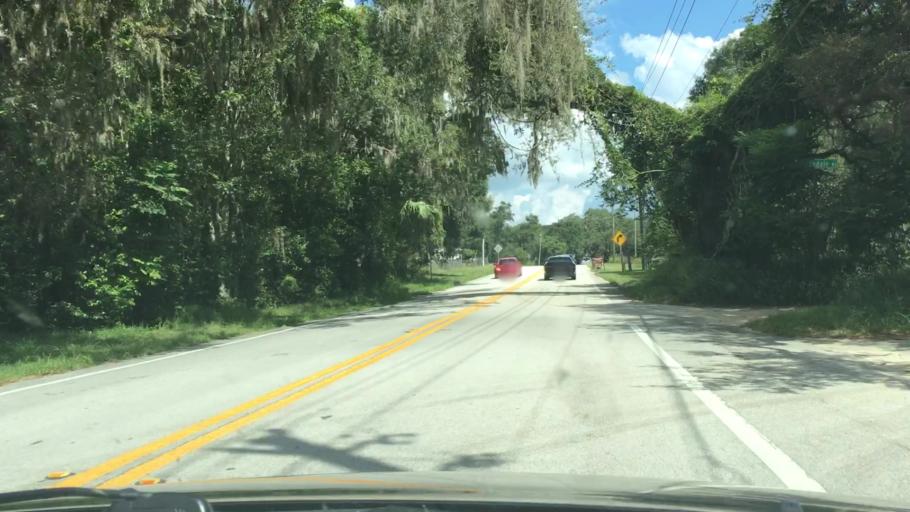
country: US
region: Florida
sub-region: Lake County
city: Montverde
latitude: 28.6200
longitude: -81.7031
